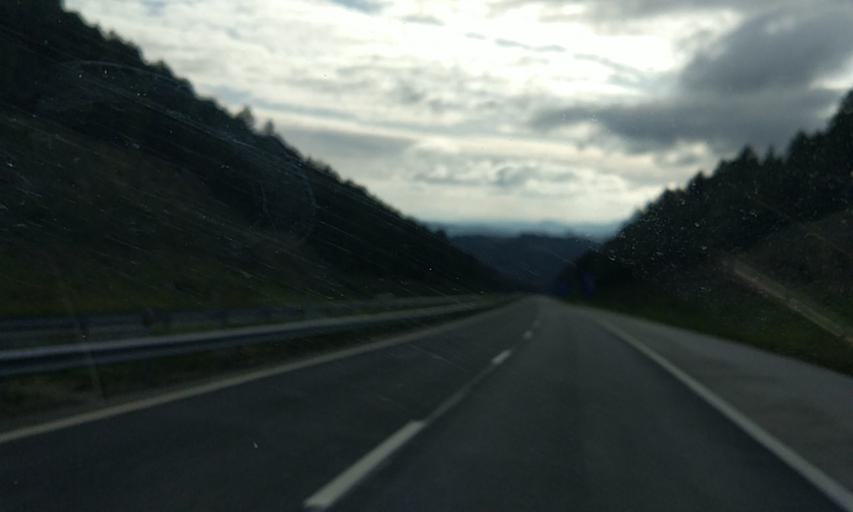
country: PT
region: Viseu
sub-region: Castro Daire
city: Castro Daire
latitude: 40.9205
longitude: -7.9147
